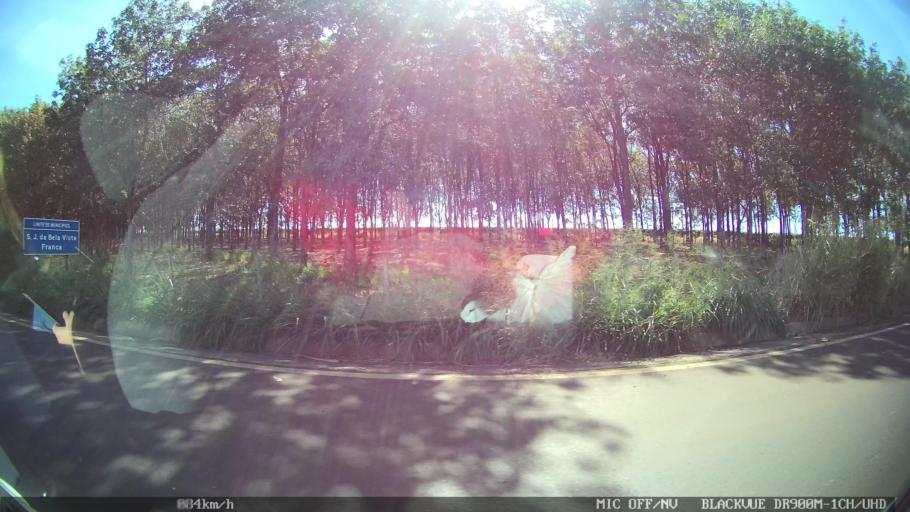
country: BR
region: Sao Paulo
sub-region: Franca
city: Franca
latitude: -20.5598
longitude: -47.5324
